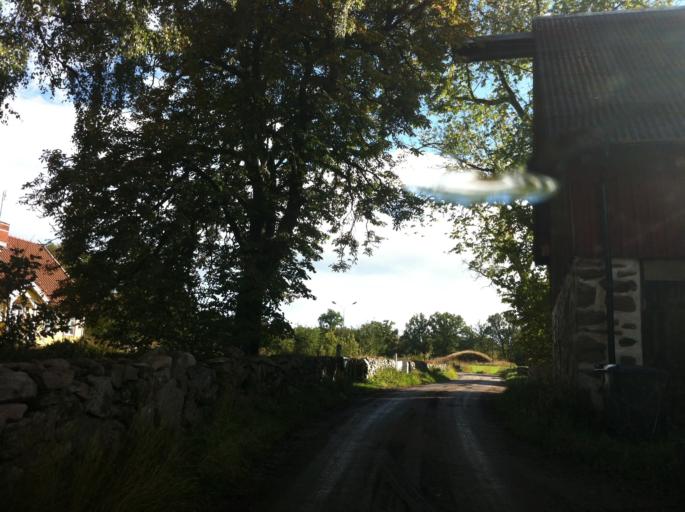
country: SE
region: Skane
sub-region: Hassleholms Kommun
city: Sosdala
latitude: 56.1234
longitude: 13.5970
